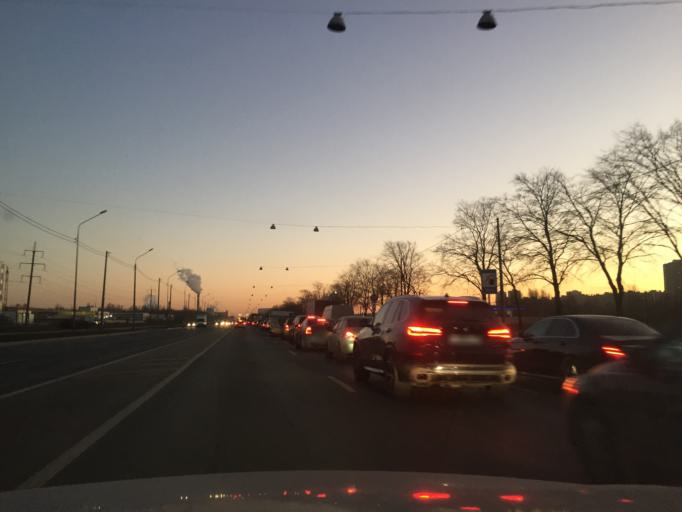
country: RU
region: St.-Petersburg
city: Obukhovo
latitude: 59.8572
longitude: 30.4222
